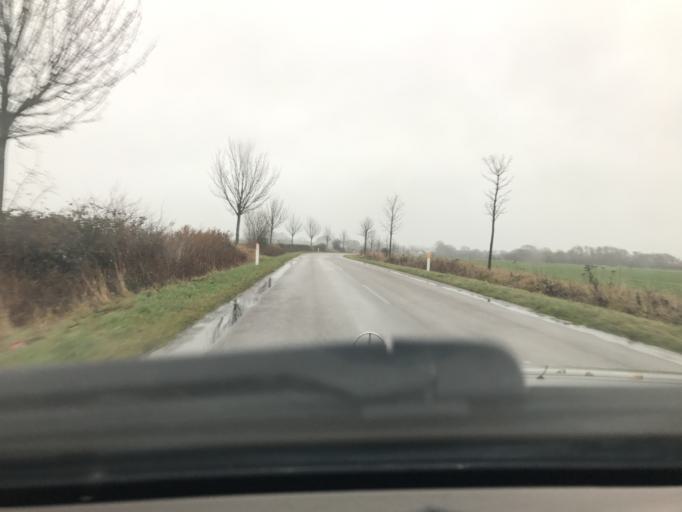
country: DK
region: South Denmark
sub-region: Sonderborg Kommune
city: Horuphav
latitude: 54.8881
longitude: 10.0061
